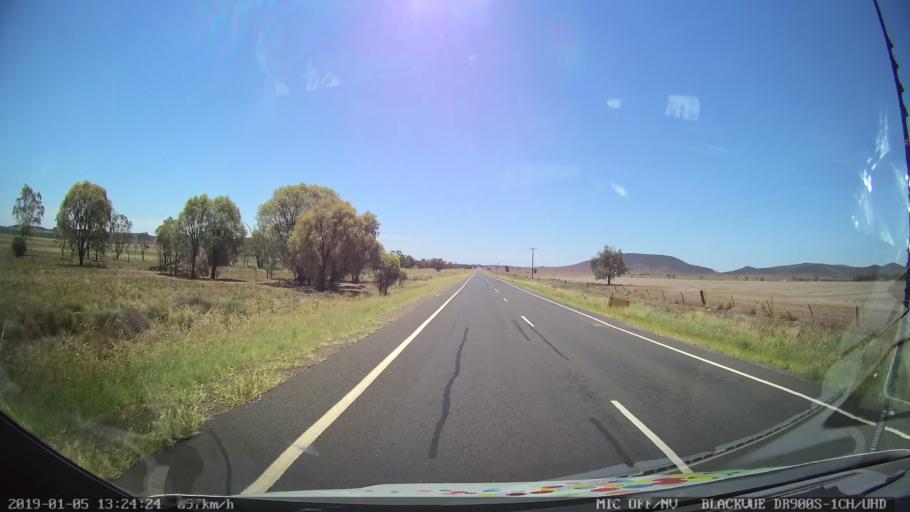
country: AU
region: New South Wales
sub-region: Gunnedah
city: Gunnedah
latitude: -31.0698
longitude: 149.9883
